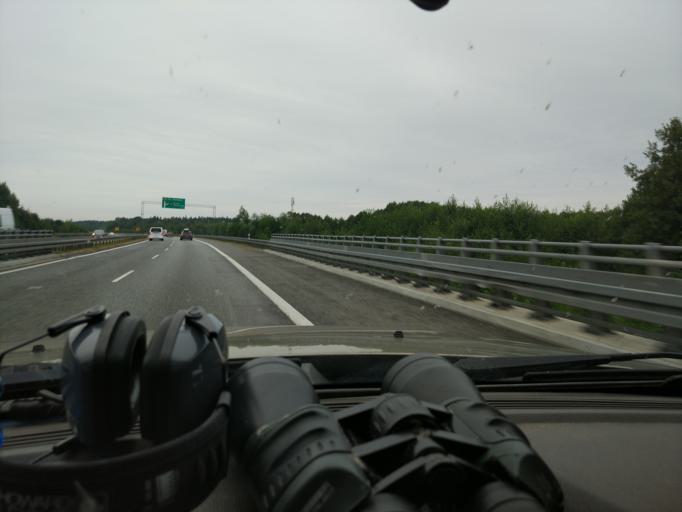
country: PL
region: Masovian Voivodeship
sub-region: Powiat wyszkowski
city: Wyszkow
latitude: 52.5801
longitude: 21.4943
